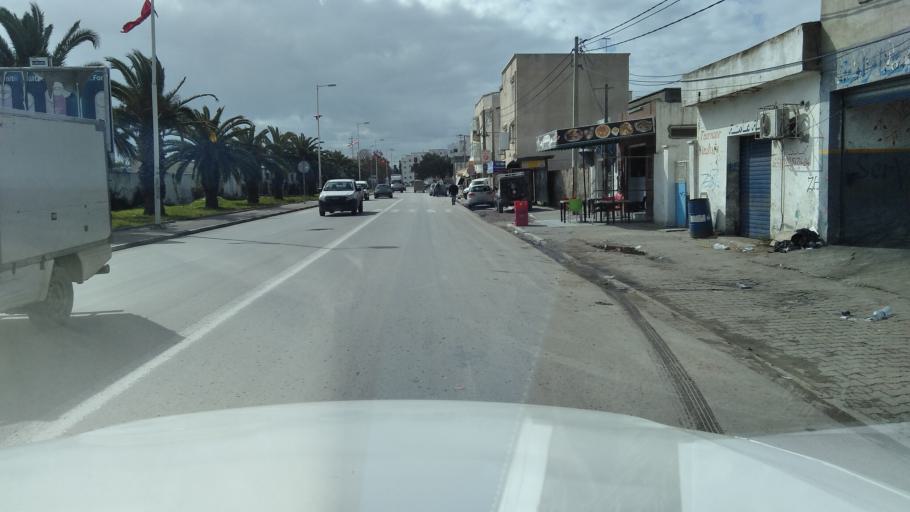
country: TN
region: Bin 'Arus
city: Ben Arous
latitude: 36.7457
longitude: 10.2259
